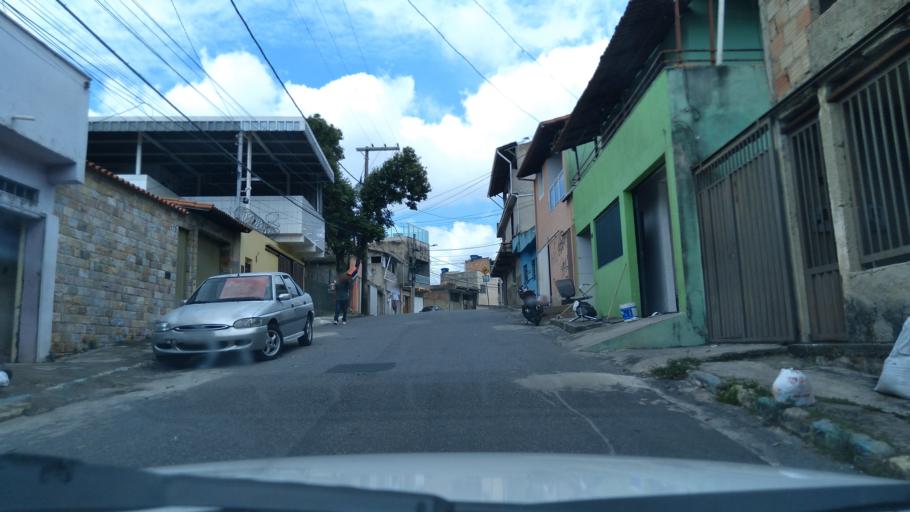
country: BR
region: Minas Gerais
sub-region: Belo Horizonte
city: Belo Horizonte
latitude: -19.8967
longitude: -43.8911
